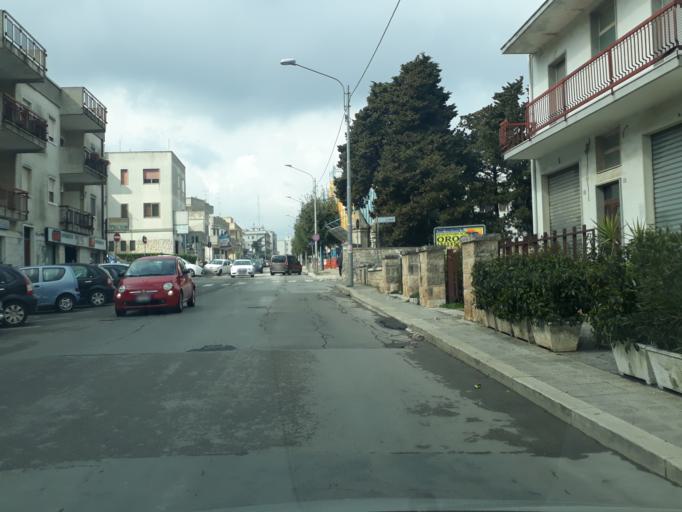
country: IT
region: Apulia
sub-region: Provincia di Bari
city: Locorotondo
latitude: 40.7541
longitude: 17.3324
